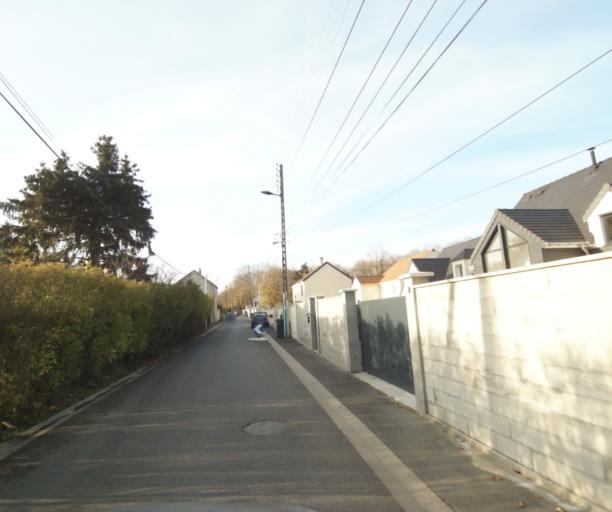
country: FR
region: Ile-de-France
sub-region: Departement des Yvelines
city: Triel-sur-Seine
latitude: 49.0007
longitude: 2.0156
